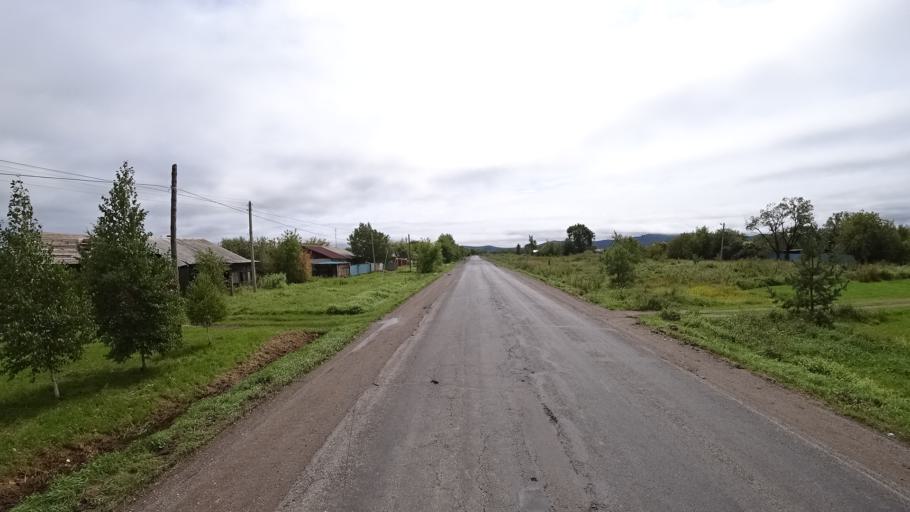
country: RU
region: Primorskiy
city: Monastyrishche
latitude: 44.1998
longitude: 132.4769
